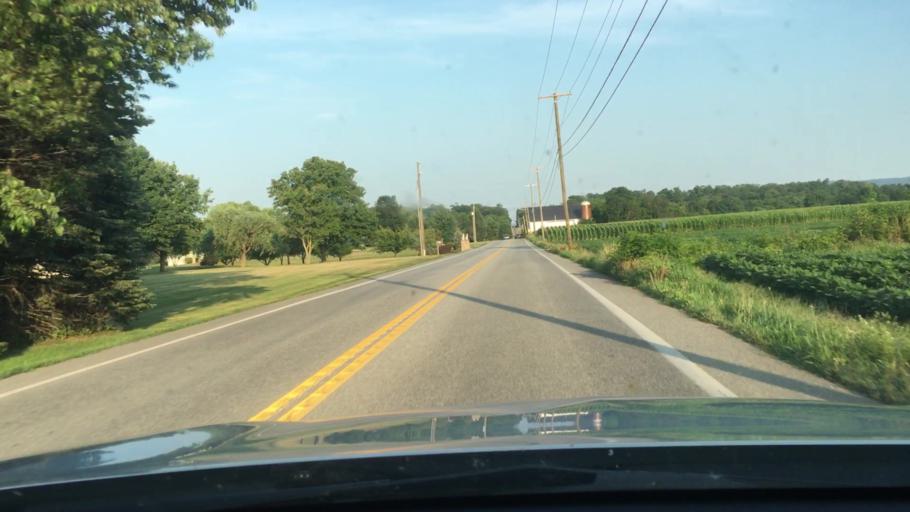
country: US
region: Pennsylvania
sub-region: Cumberland County
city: Boiling Springs
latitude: 40.1764
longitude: -77.1284
